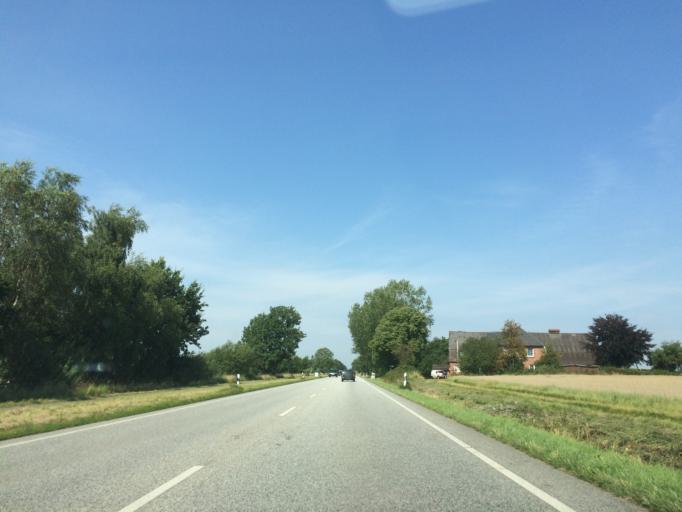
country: DE
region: Schleswig-Holstein
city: Neudorf-Bornstein
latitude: 54.4260
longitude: 9.9591
